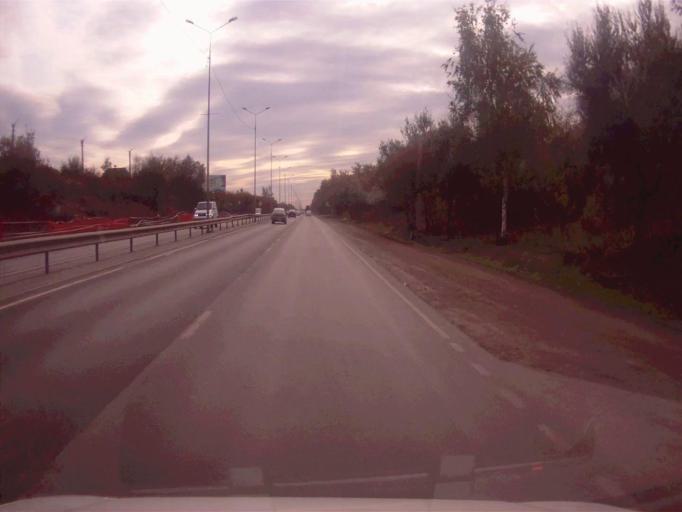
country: RU
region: Chelyabinsk
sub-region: Gorod Chelyabinsk
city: Chelyabinsk
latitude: 55.1062
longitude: 61.4073
